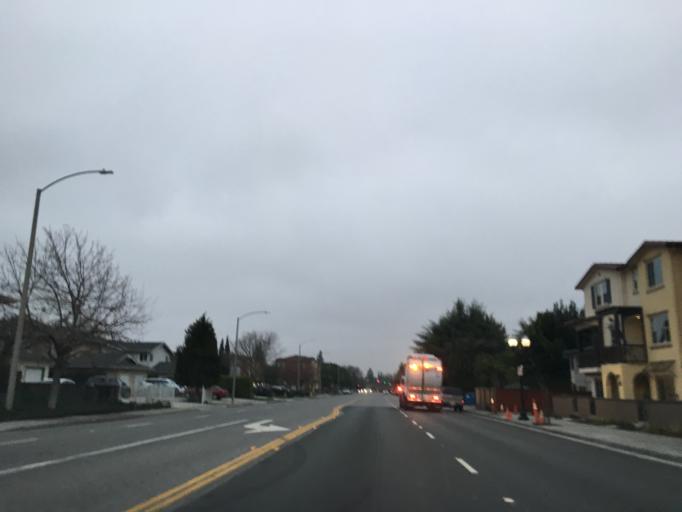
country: US
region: California
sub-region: Santa Clara County
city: Sunnyvale
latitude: 37.3822
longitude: -122.0182
